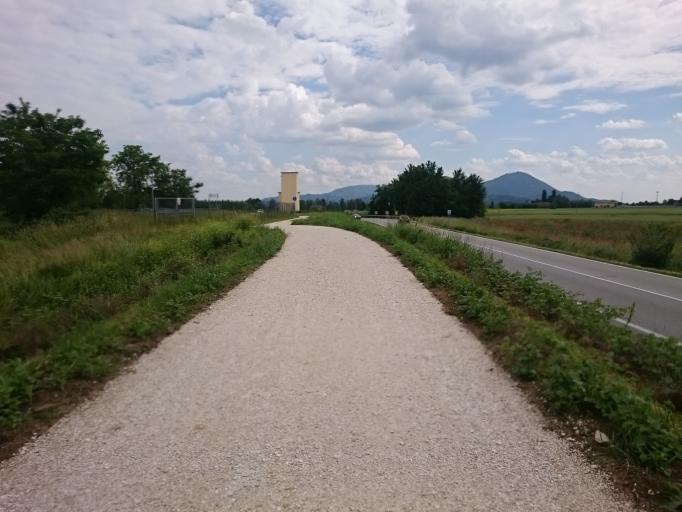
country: IT
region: Veneto
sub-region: Provincia di Vicenza
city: Montegaldella
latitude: 45.4304
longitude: 11.6775
